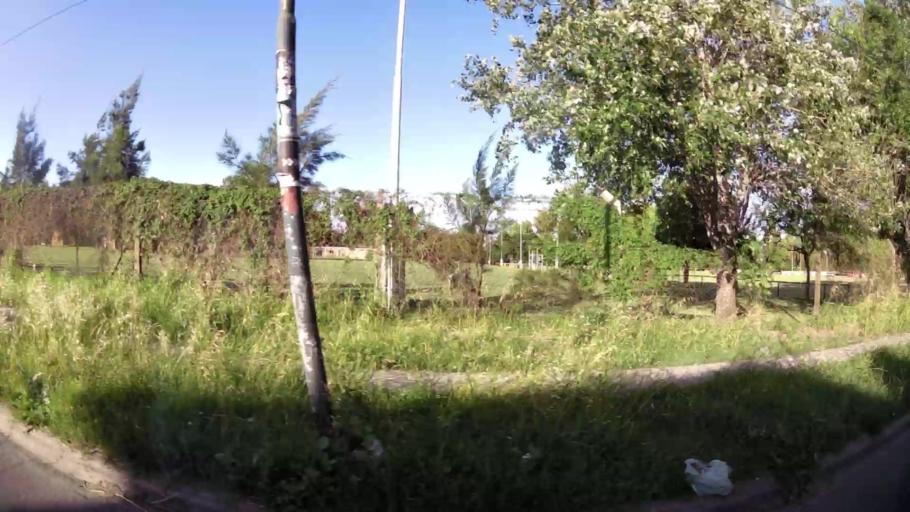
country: AR
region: Buenos Aires
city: Caseros
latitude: -34.5702
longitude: -58.5889
